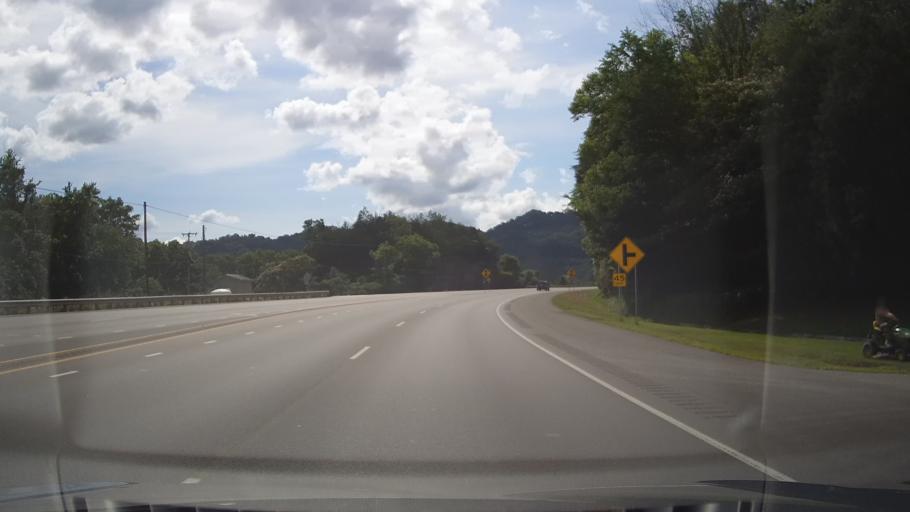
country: US
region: Kentucky
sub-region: Floyd County
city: Prestonsburg
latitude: 37.6134
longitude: -82.7163
